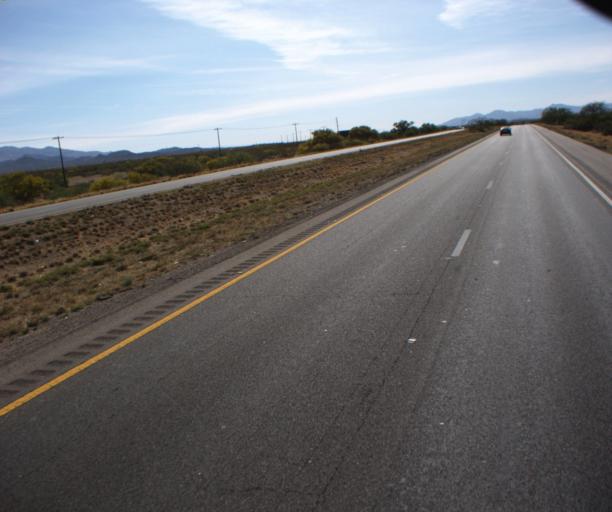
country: US
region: Arizona
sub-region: Pima County
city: Vail
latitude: 32.0495
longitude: -110.7548
